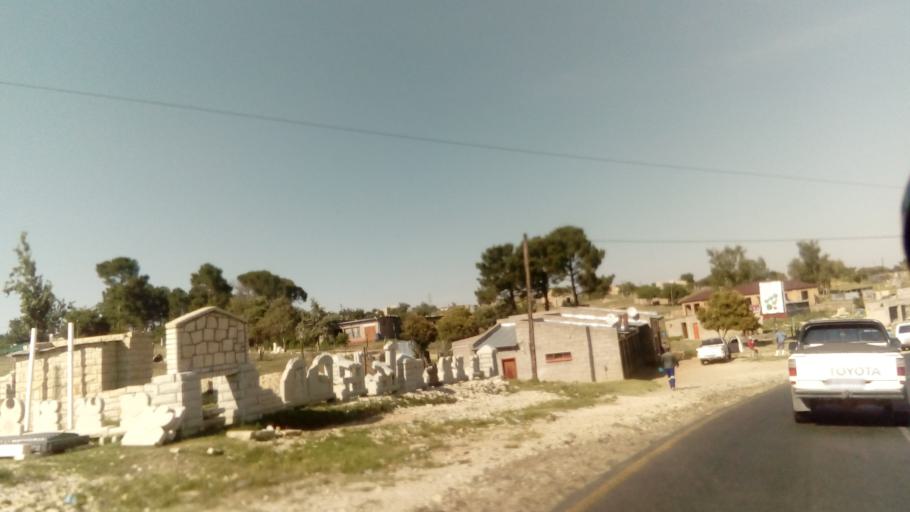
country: LS
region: Berea
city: Teyateyaneng
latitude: -29.1582
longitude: 27.6804
